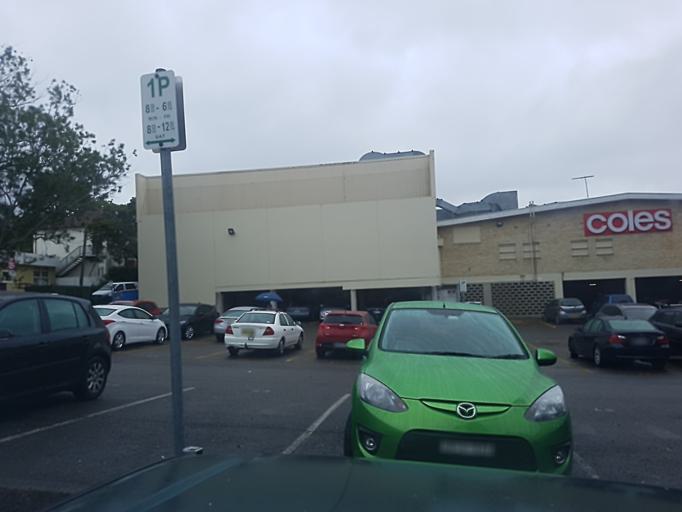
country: AU
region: New South Wales
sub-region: City of Sydney
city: Pymble
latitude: -33.7328
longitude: 151.1278
